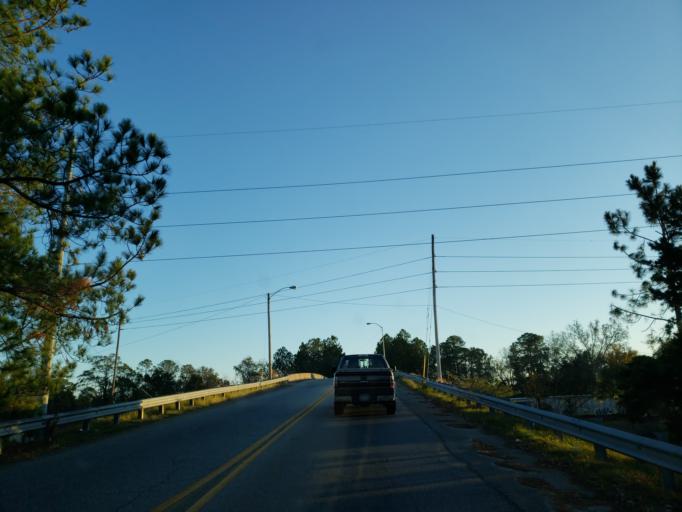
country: US
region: Georgia
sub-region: Crisp County
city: Cordele
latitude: 31.9711
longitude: -83.7796
